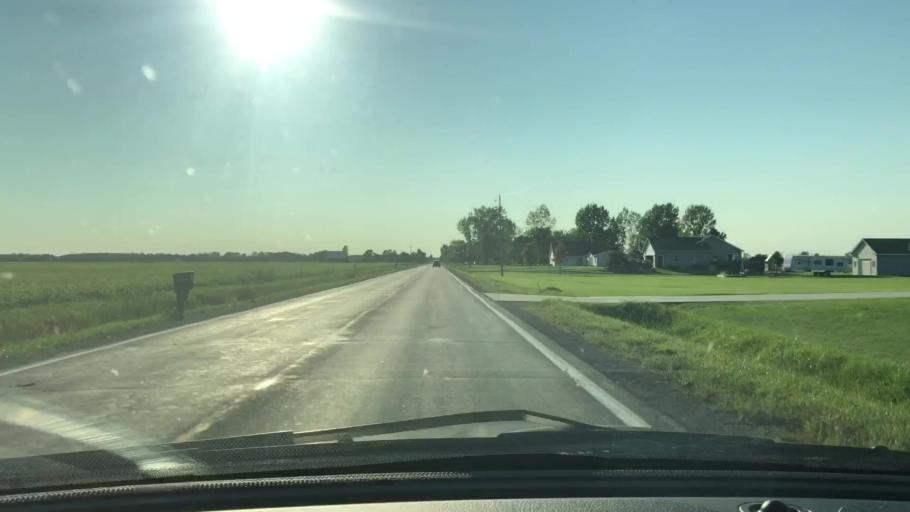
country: US
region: Michigan
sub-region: Bay County
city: Auburn
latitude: 43.6401
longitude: -84.1096
